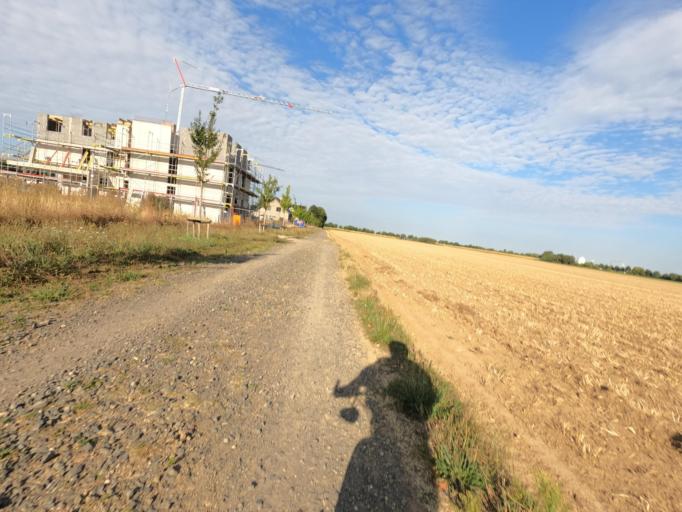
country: DE
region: North Rhine-Westphalia
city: Erkelenz
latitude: 51.0831
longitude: 6.2919
